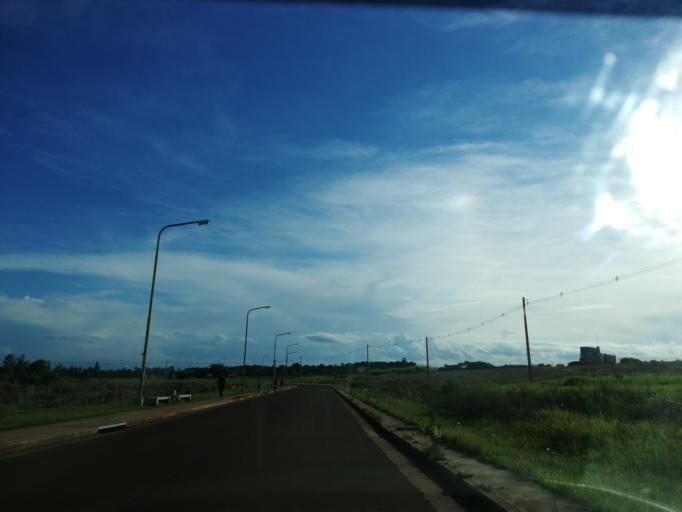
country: AR
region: Misiones
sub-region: Departamento de Capital
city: Posadas
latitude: -27.3928
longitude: -55.9552
